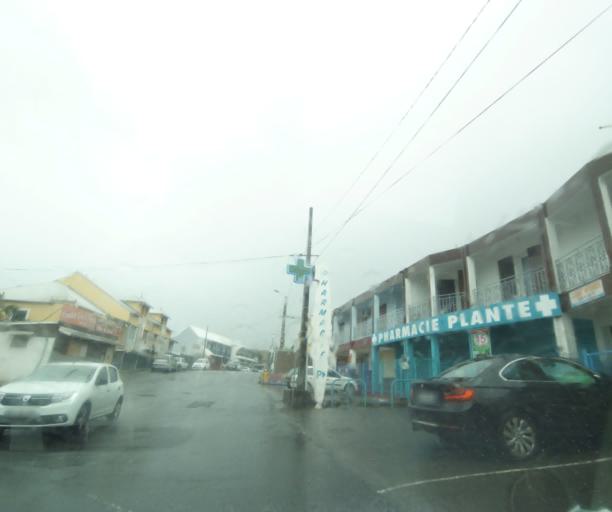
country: RE
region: Reunion
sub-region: Reunion
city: La Possession
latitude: -20.9834
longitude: 55.3264
